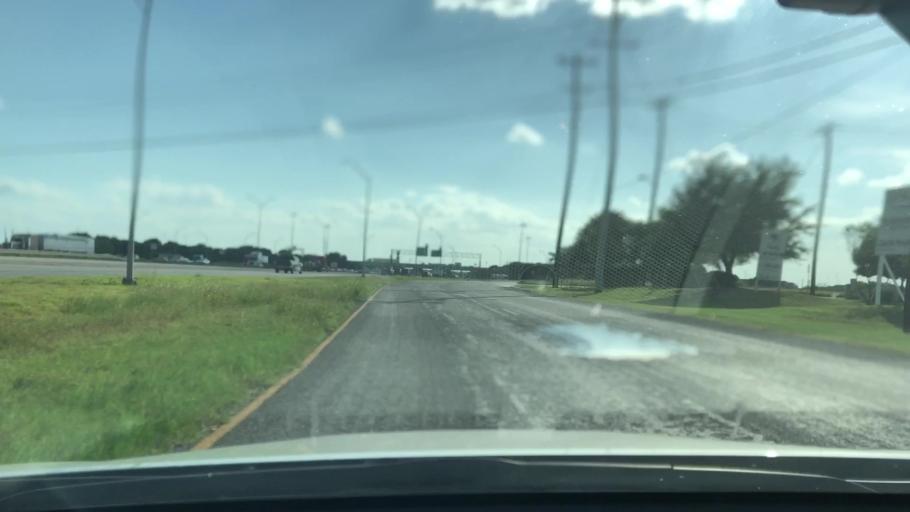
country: US
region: Texas
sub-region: Bexar County
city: Kirby
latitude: 29.4383
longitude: -98.3855
